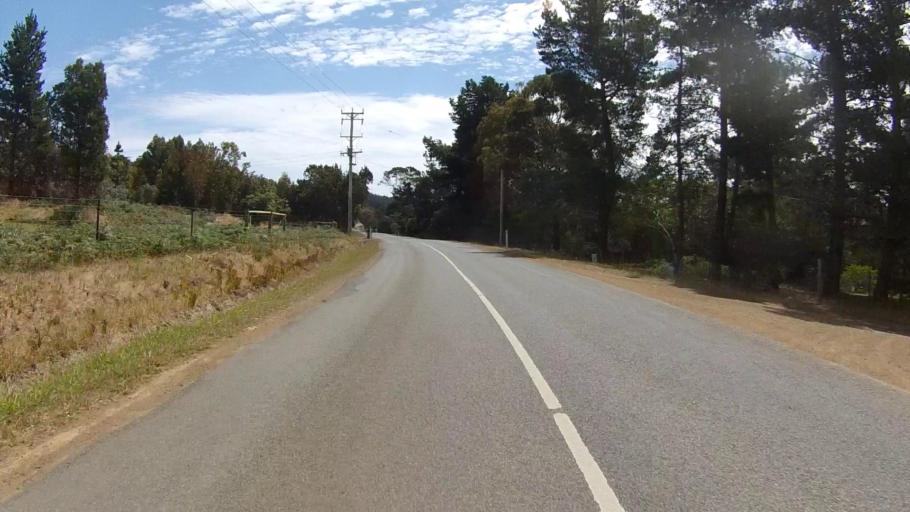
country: AU
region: Tasmania
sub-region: Clarence
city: Sandford
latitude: -42.9855
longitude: 147.5170
